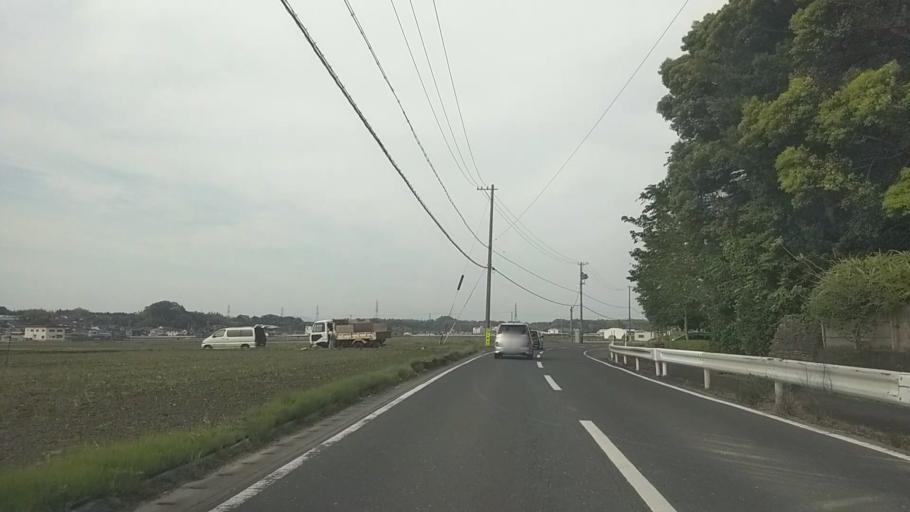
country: JP
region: Shizuoka
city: Hamamatsu
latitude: 34.7364
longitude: 137.6433
